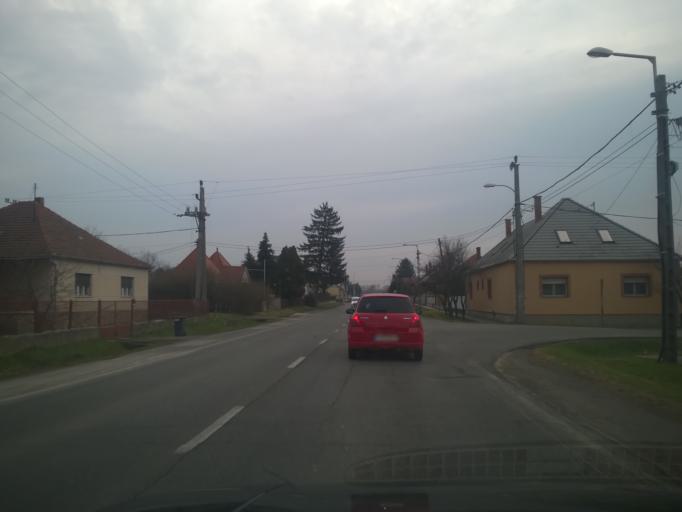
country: HU
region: Baranya
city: Szentlorinc
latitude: 46.0446
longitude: 17.9837
